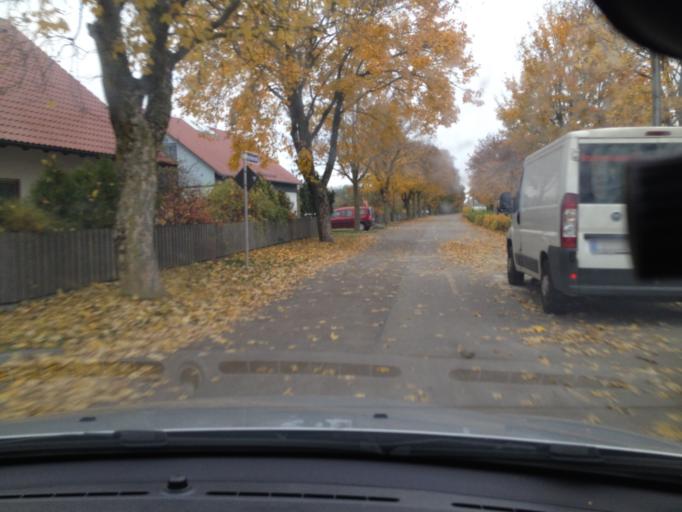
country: DE
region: Bavaria
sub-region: Swabia
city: Kleinaitingen
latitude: 48.2152
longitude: 10.8440
